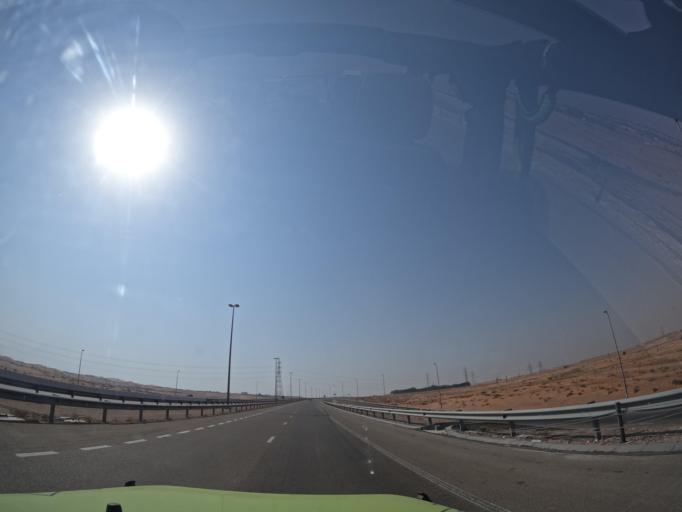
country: OM
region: Al Buraimi
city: Al Buraymi
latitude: 24.3876
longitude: 55.7251
